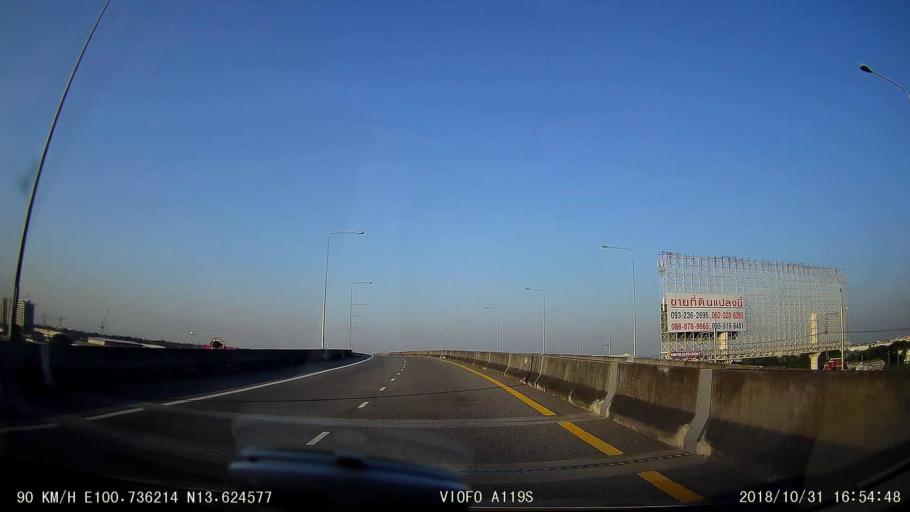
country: TH
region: Samut Prakan
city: Bang Bo District
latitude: 13.6249
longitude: 100.7363
